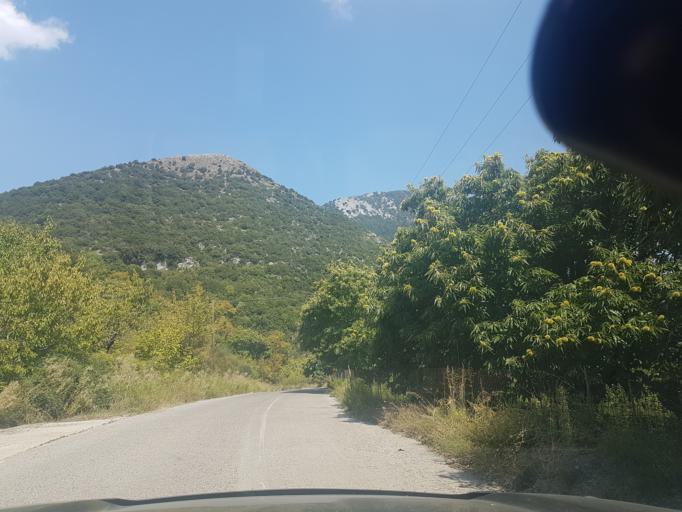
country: GR
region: Central Greece
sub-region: Nomos Evvoias
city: Kymi
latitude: 38.6453
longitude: 23.8998
